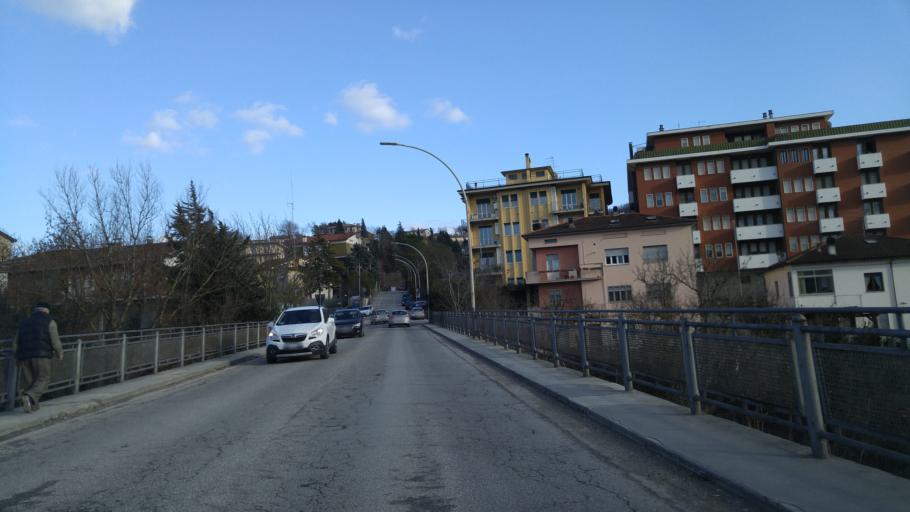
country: IT
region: The Marches
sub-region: Provincia di Pesaro e Urbino
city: Cagli
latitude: 43.5456
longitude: 12.6514
